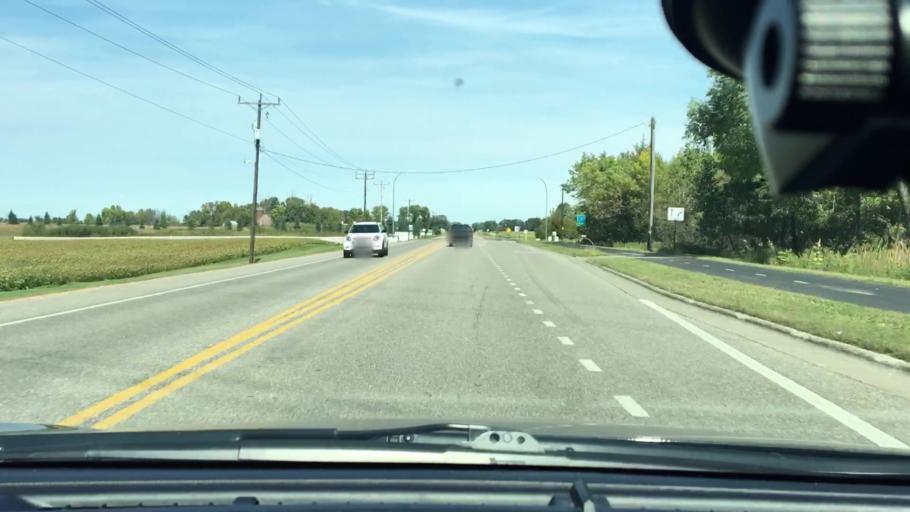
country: US
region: Minnesota
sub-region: Wright County
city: Hanover
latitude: 45.1295
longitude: -93.6357
